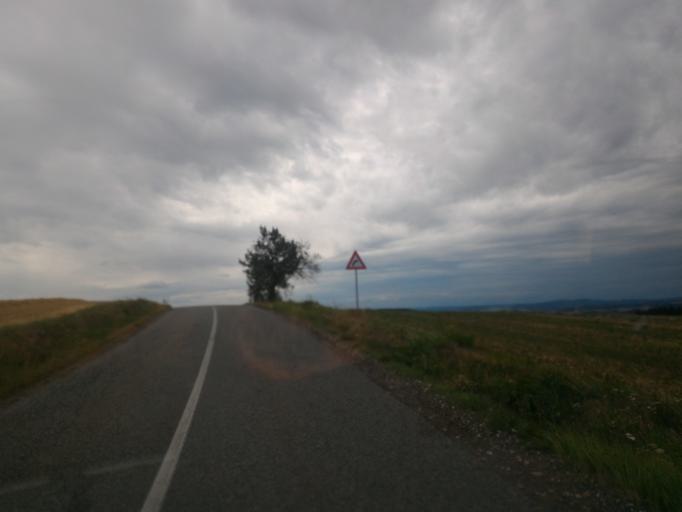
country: CZ
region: Vysocina
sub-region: Okres Jihlava
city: Trest'
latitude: 49.2384
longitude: 15.5562
